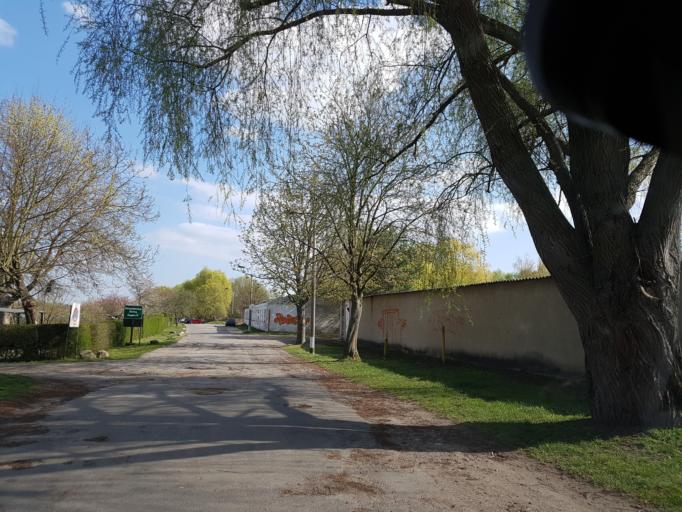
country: DE
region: Brandenburg
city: Juterbog
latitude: 51.9940
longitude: 13.0513
